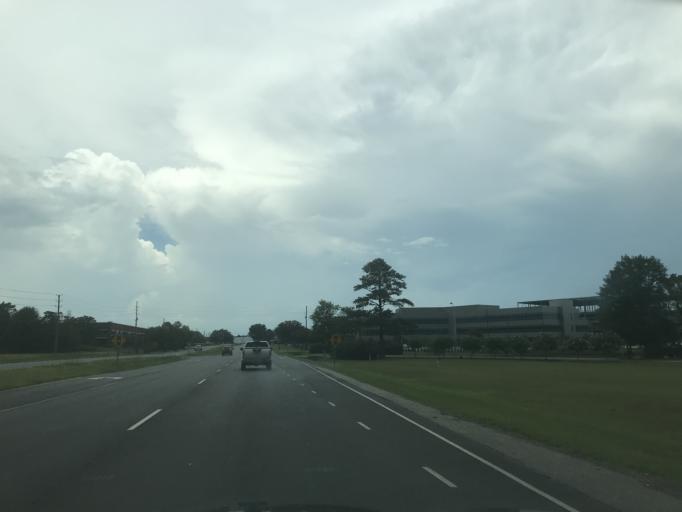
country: US
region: North Carolina
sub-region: Johnston County
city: Clayton
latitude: 35.6162
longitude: -78.4189
